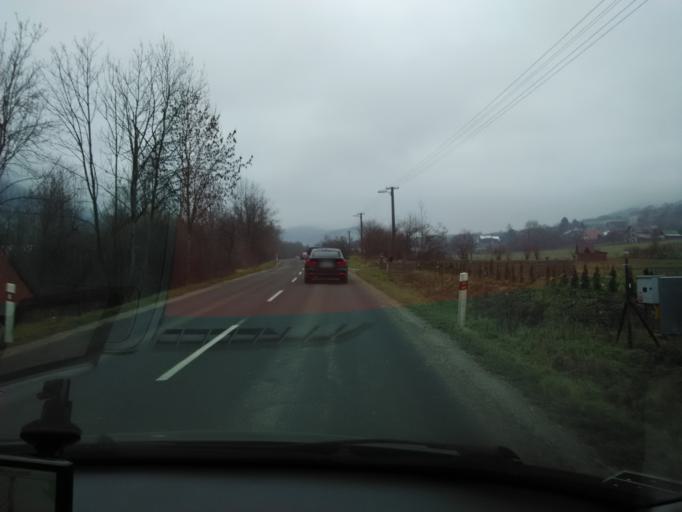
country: SK
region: Zilinsky
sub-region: Okres Zilina
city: Terchova
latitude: 49.2511
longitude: 19.0048
